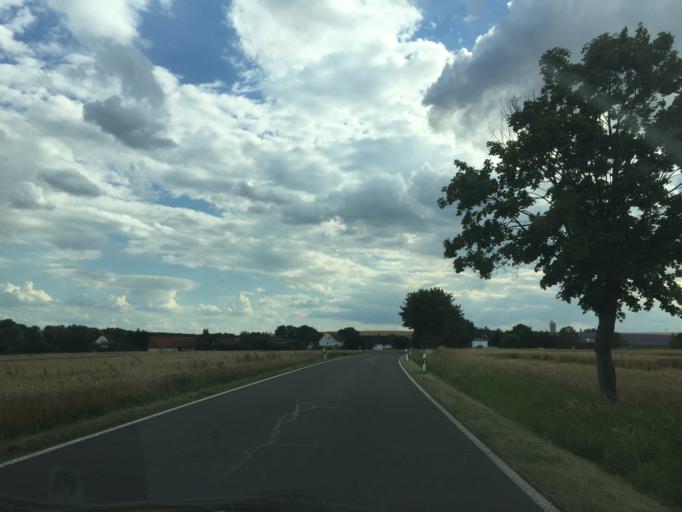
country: DE
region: Thuringia
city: Saara
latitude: 50.9442
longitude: 12.4184
